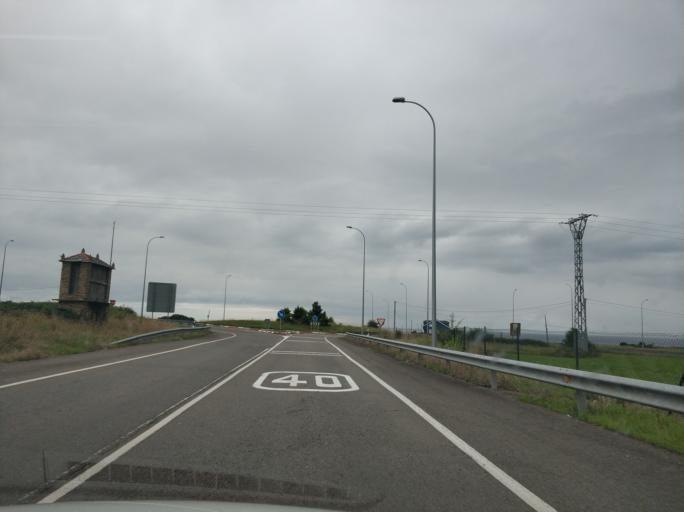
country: ES
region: Galicia
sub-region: Provincia de Lugo
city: Barreiros
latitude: 43.5464
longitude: -7.1515
